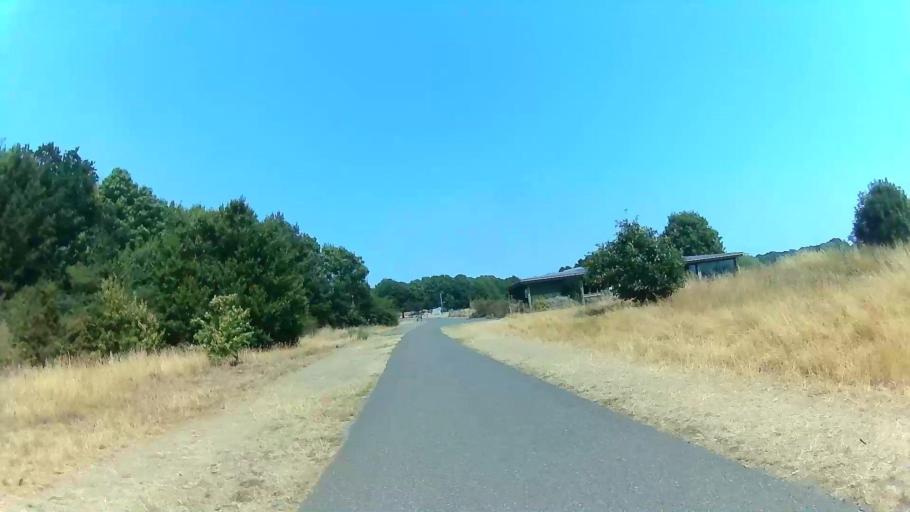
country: GB
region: England
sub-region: Greater London
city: Elm Park
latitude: 51.5405
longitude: 0.2143
